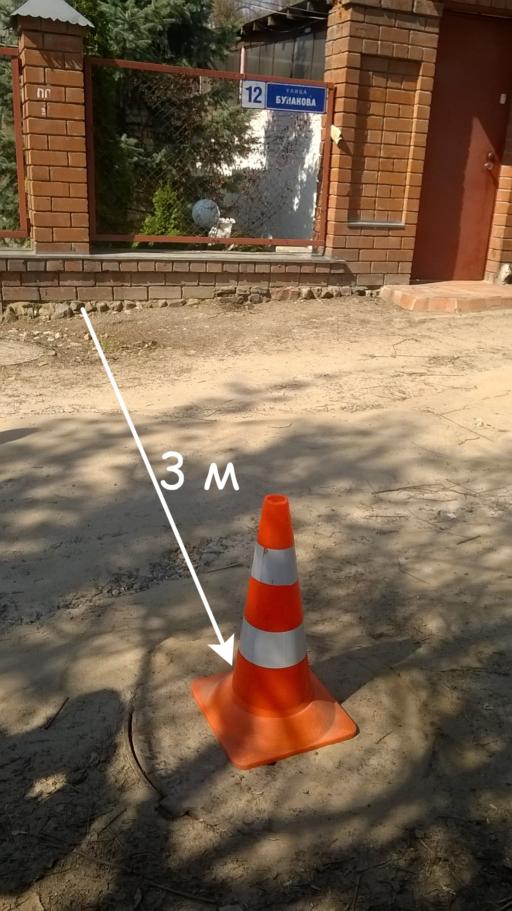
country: RU
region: Voronezj
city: Voronezh
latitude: 51.7084
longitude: 39.2317
